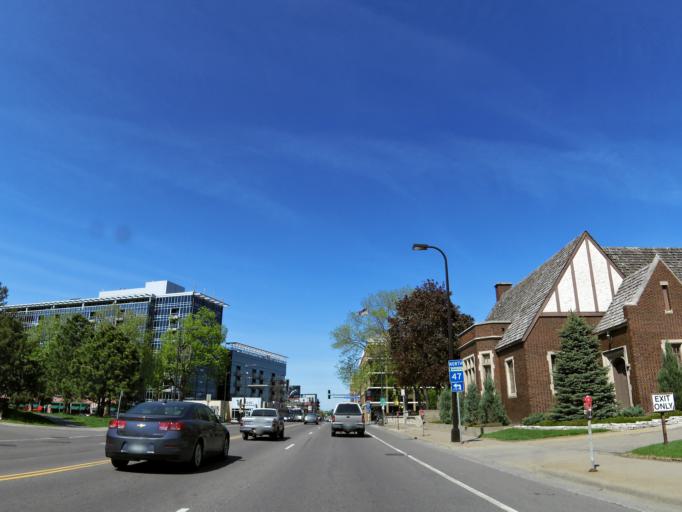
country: US
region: Minnesota
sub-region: Hennepin County
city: Minneapolis
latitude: 44.9860
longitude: -93.2554
